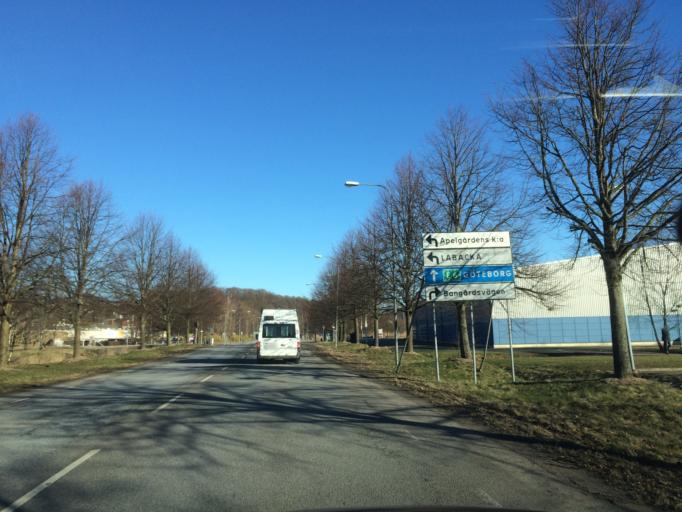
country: SE
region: Vaestra Goetaland
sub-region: Molndal
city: Kallered
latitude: 57.6085
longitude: 12.0435
